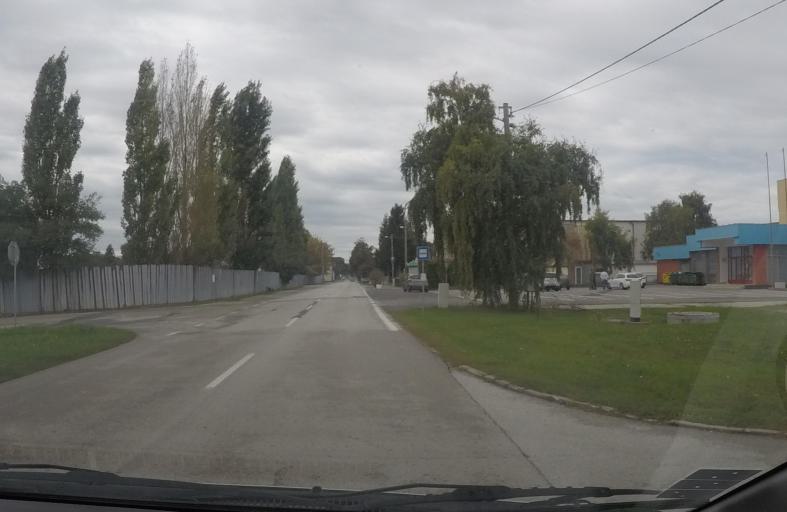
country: SK
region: Trnavsky
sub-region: Okres Galanta
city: Galanta
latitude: 48.1953
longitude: 17.7427
